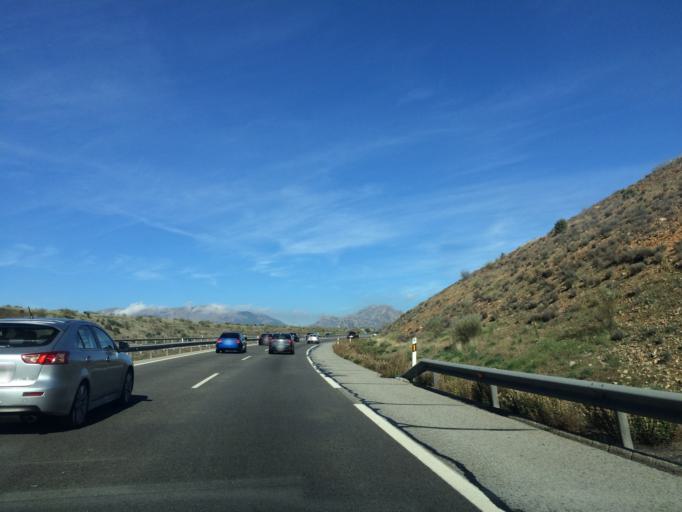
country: ES
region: Madrid
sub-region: Provincia de Madrid
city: Venturada
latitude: 40.8057
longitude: -3.6192
